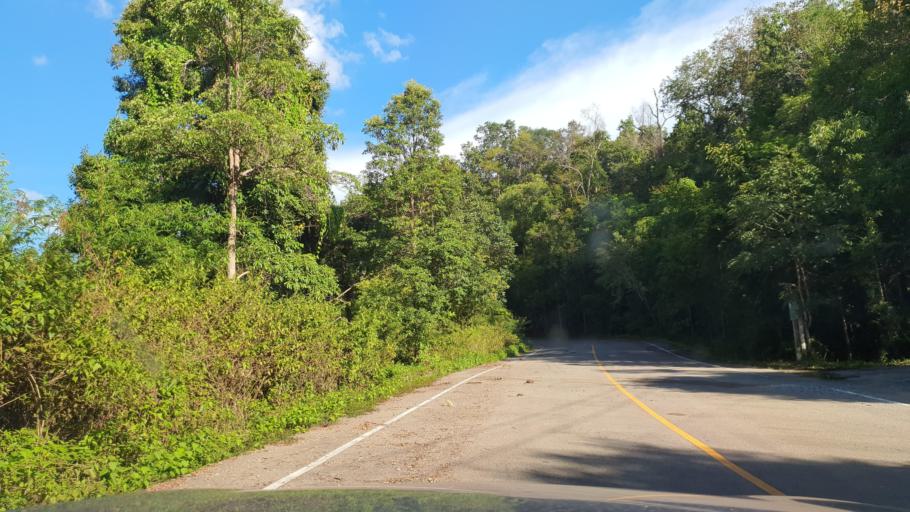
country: TH
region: Chiang Mai
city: Mae On
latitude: 18.7892
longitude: 99.3038
